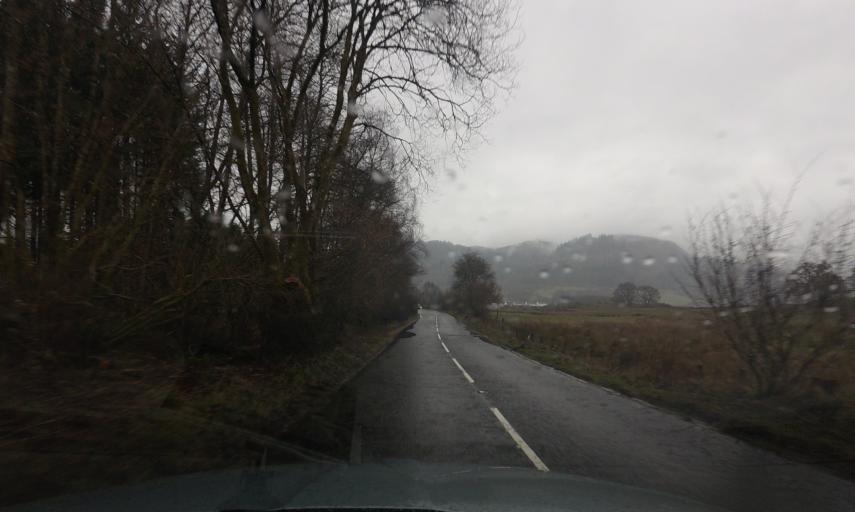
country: GB
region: Scotland
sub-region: Stirling
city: Balfron
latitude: 56.1664
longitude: -4.3648
